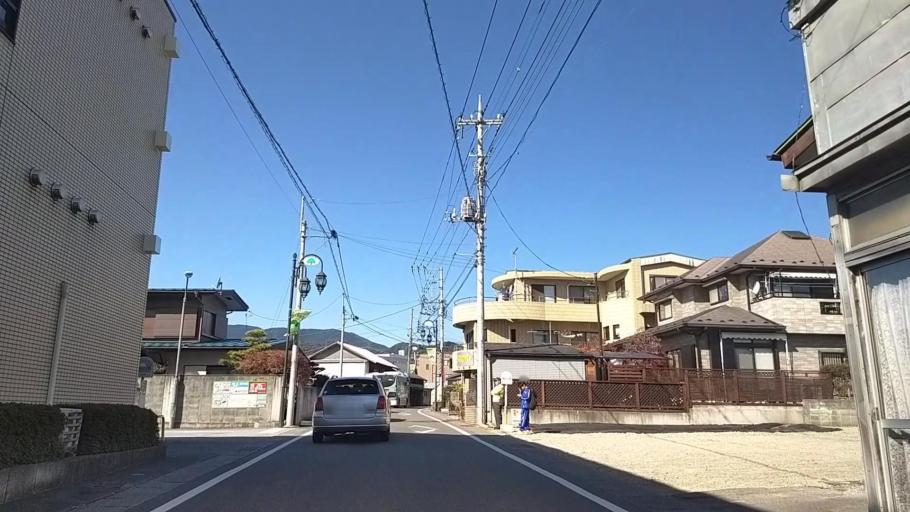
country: JP
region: Yamanashi
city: Uenohara
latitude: 35.6293
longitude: 139.1112
